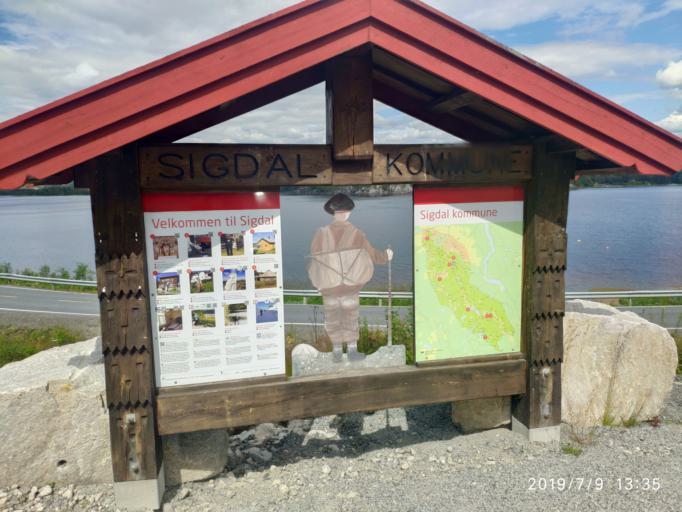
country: NO
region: Buskerud
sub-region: Sigdal
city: Prestfoss
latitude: 60.0614
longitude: 9.5073
